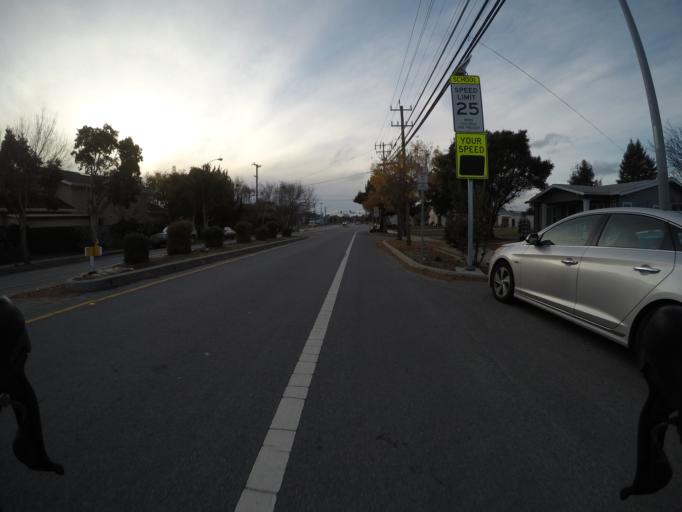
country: US
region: California
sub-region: Santa Cruz County
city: Live Oak
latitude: 36.9755
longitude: -121.9789
